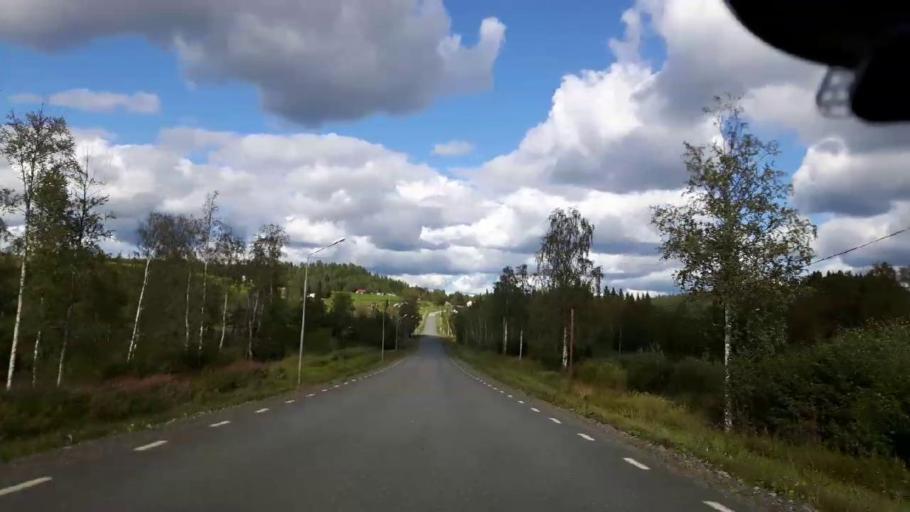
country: SE
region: Jaemtland
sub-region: Stroemsunds Kommun
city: Stroemsund
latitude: 63.2921
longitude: 15.5919
